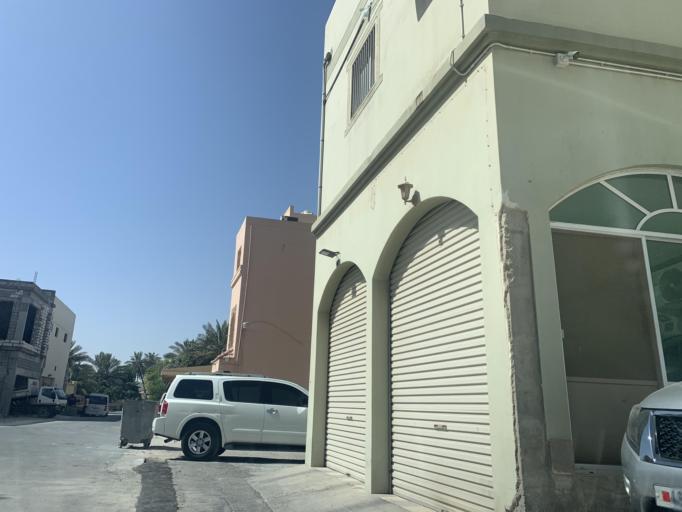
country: BH
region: Manama
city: Jidd Hafs
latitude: 26.2258
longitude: 50.5310
